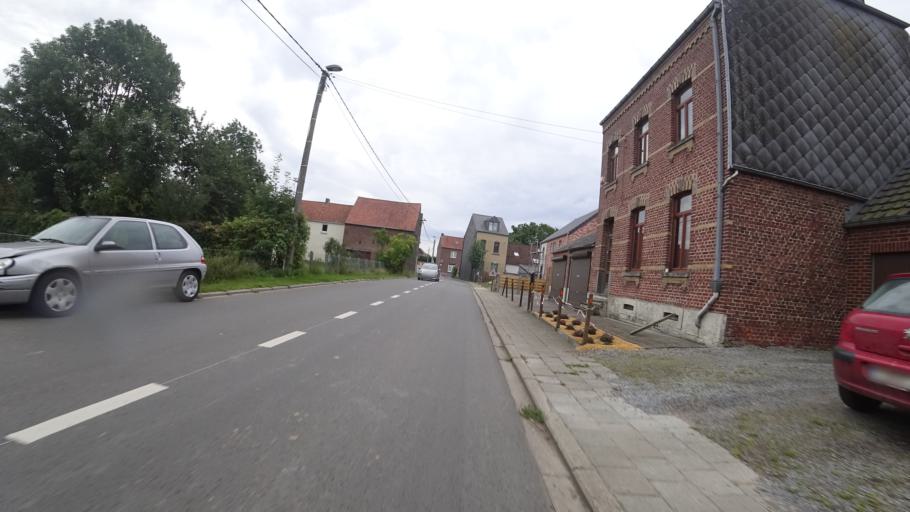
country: BE
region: Wallonia
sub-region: Province du Brabant Wallon
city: Walhain-Saint-Paul
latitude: 50.6132
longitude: 4.7203
